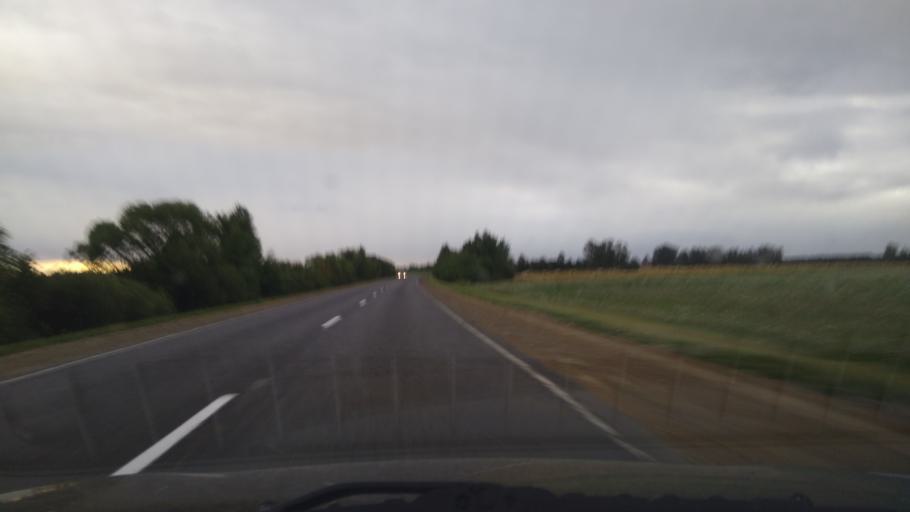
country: BY
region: Brest
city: Byaroza
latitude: 52.4452
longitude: 24.9732
